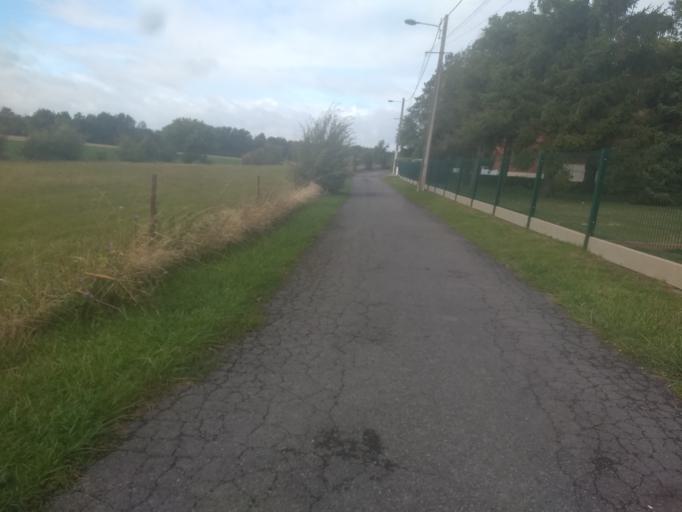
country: FR
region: Nord-Pas-de-Calais
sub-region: Departement du Pas-de-Calais
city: Dainville
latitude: 50.2811
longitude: 2.7143
